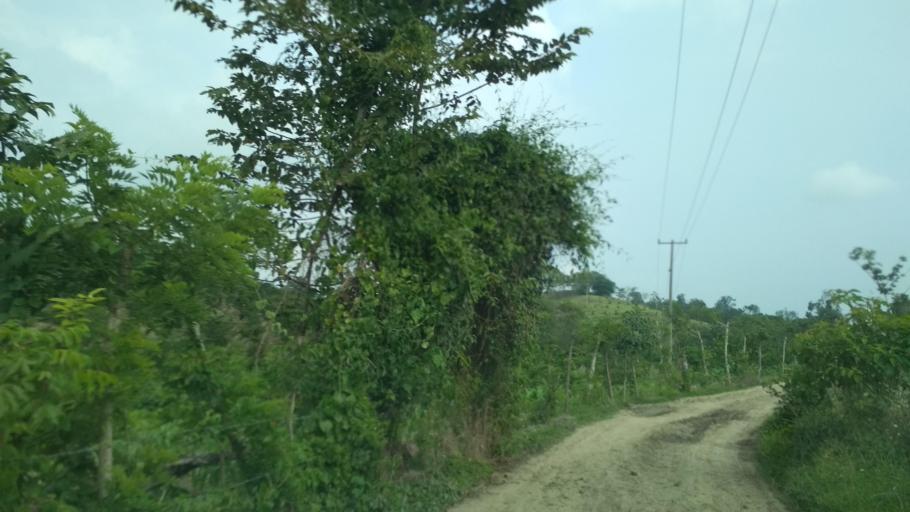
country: MM
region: Kayah
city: Loikaw
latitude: 20.2133
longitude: 97.3154
